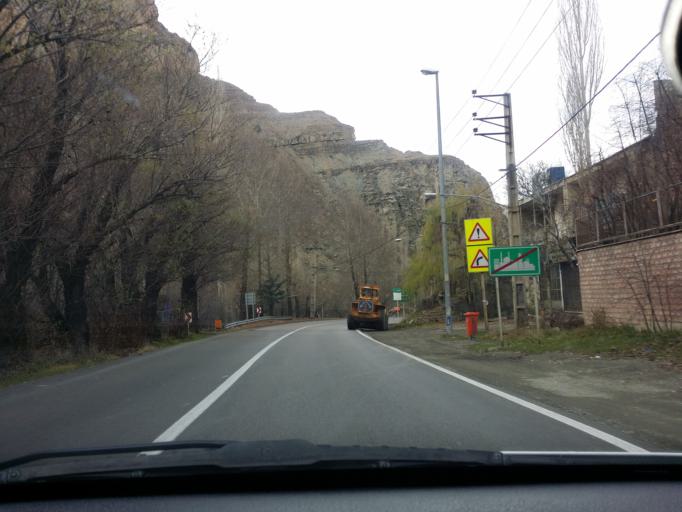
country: IR
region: Alborz
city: Karaj
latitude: 36.0241
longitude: 51.1559
